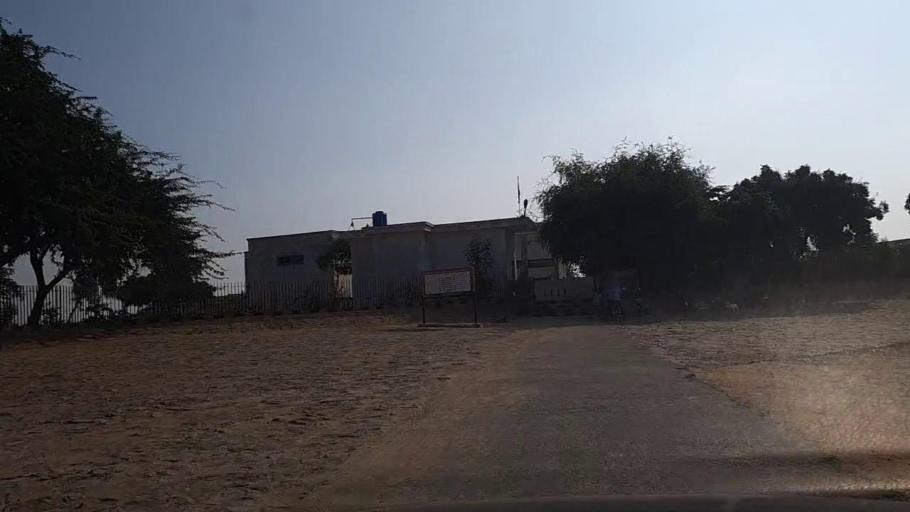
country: PK
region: Sindh
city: Gharo
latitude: 24.7556
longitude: 67.5235
